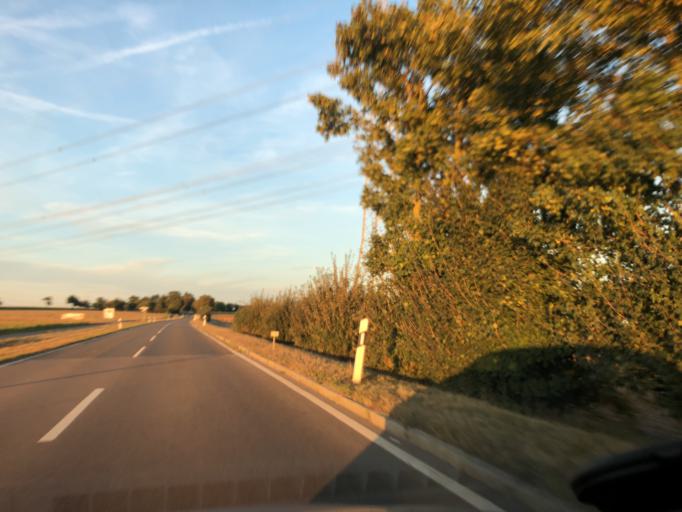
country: DE
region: Baden-Wuerttemberg
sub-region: Regierungsbezirk Stuttgart
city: Benningen am Neckar
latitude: 48.9151
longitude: 9.2371
